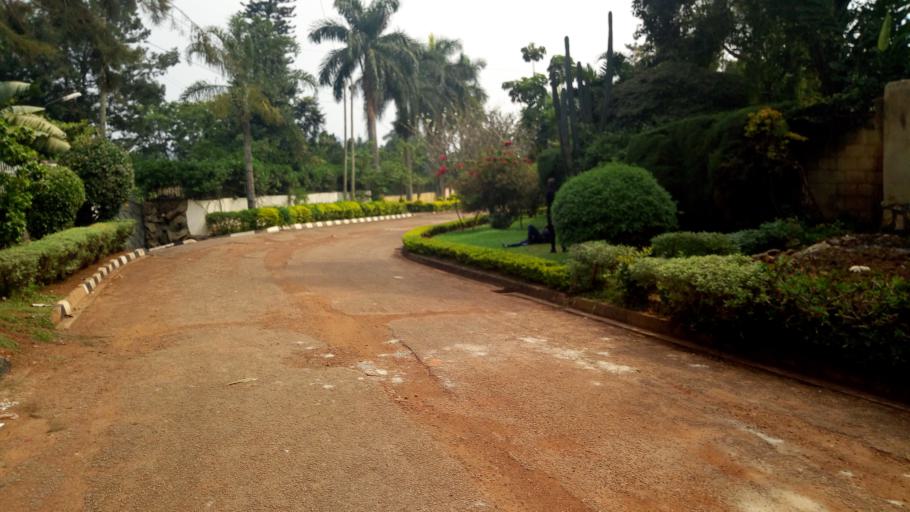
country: UG
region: Central Region
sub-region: Kampala District
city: Kampala
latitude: 0.3096
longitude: 32.6248
